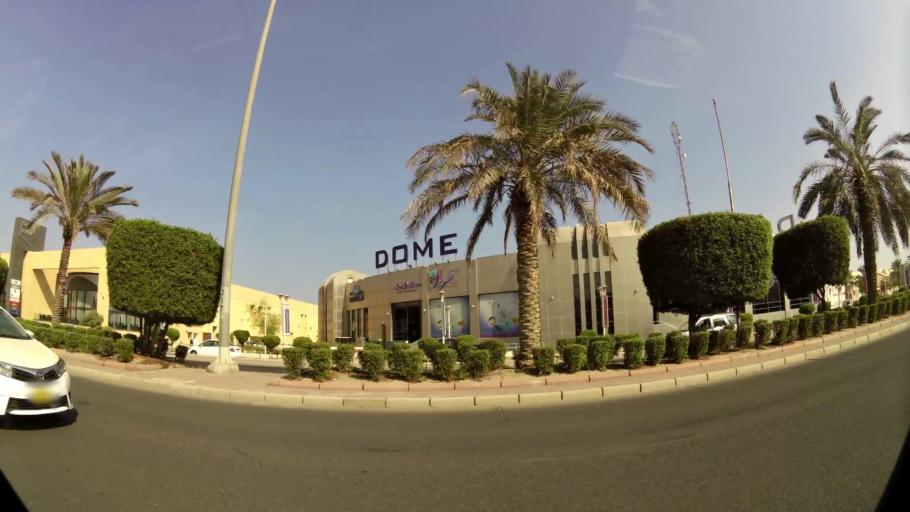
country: KW
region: Al Ahmadi
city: Al Mahbulah
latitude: 29.1355
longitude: 48.1306
